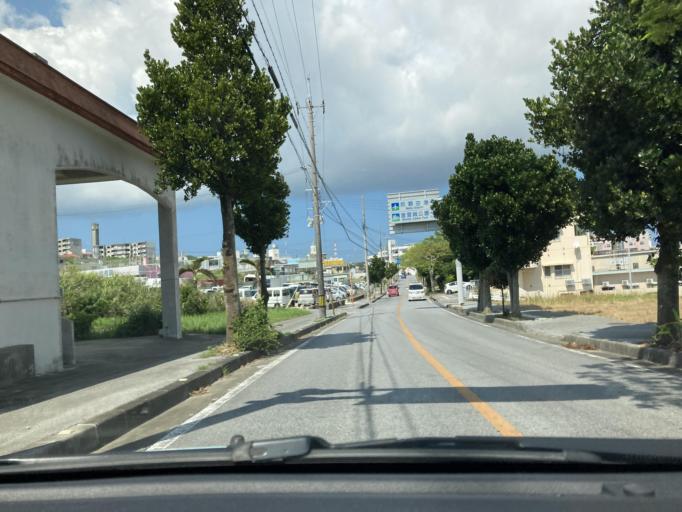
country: JP
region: Okinawa
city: Tomigusuku
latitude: 26.1749
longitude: 127.7213
